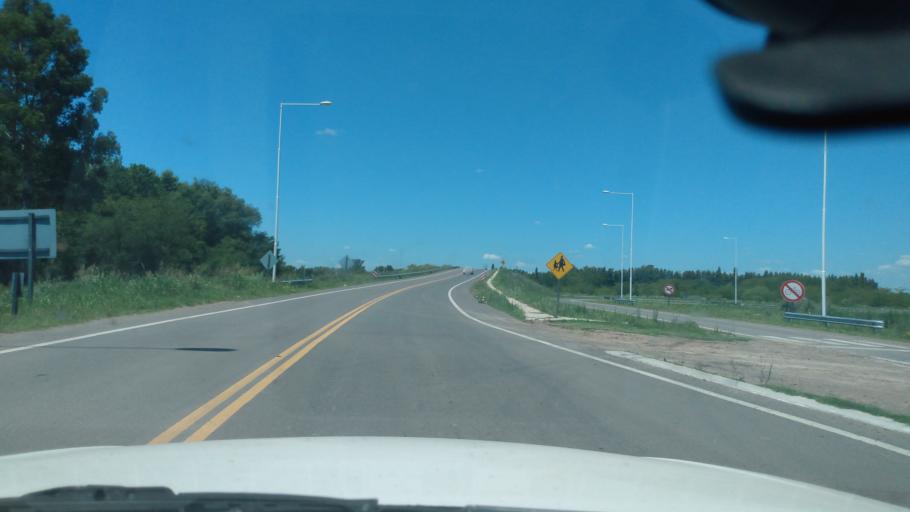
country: AR
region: Buenos Aires
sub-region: Partido de San Andres de Giles
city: San Andres de Giles
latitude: -34.4600
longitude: -59.4171
